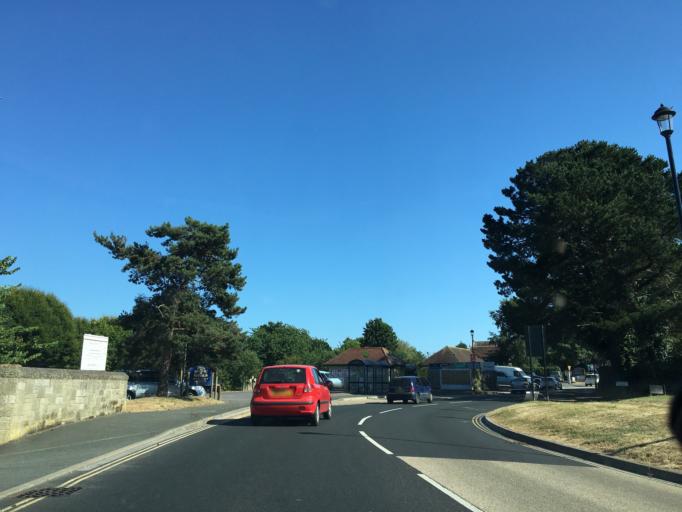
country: GB
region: England
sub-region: Isle of Wight
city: Brading
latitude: 50.6837
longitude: -1.1434
